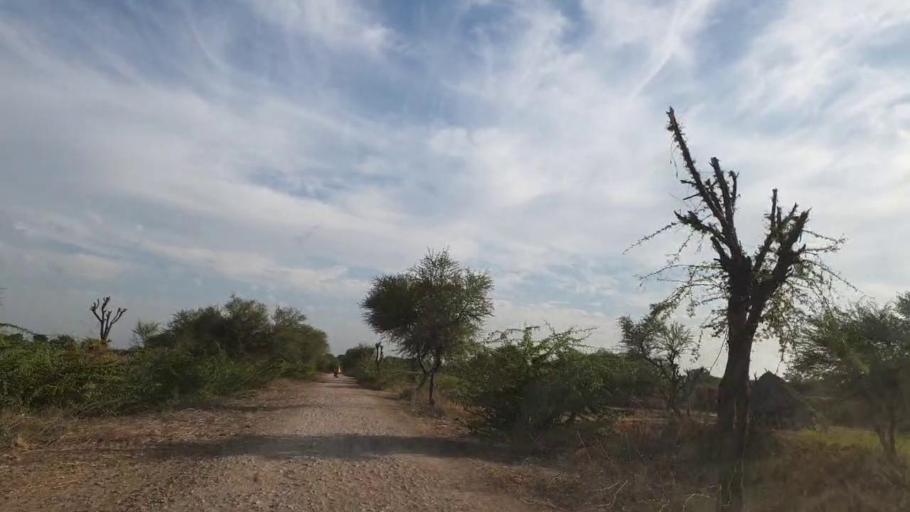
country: PK
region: Sindh
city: Pithoro
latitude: 25.6453
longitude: 69.2915
